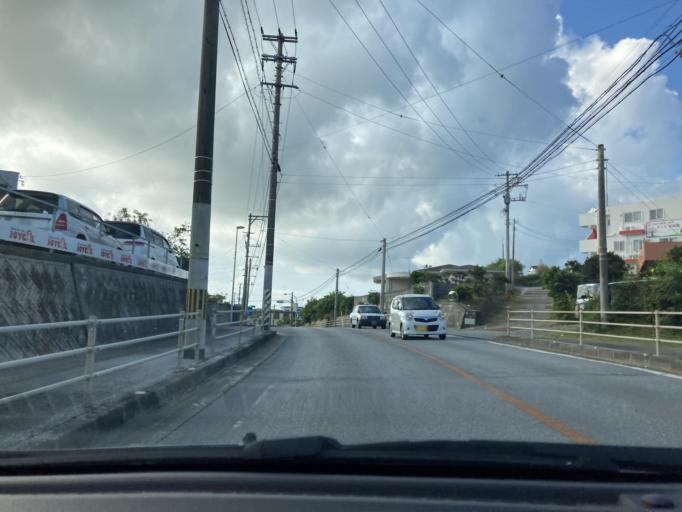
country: JP
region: Okinawa
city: Tomigusuku
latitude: 26.1652
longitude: 127.7392
